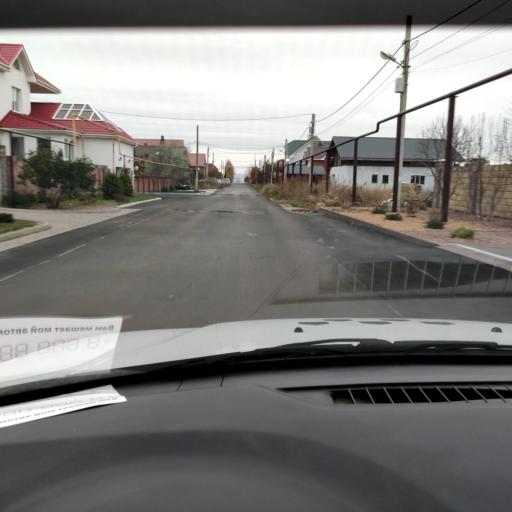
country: RU
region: Samara
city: Podstepki
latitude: 53.5141
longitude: 49.2076
